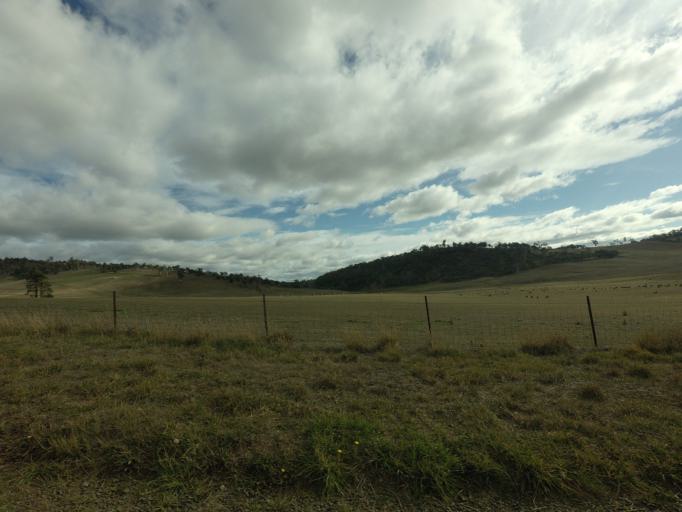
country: AU
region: Tasmania
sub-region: Brighton
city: Bridgewater
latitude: -42.4676
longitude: 147.2796
